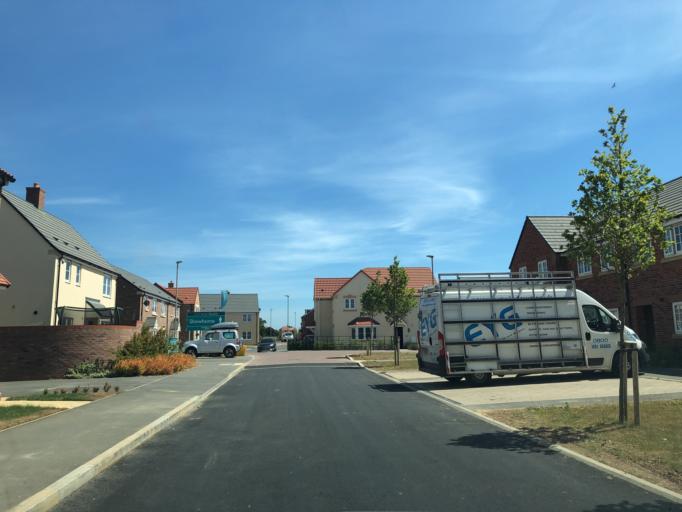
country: GB
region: England
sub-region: North Yorkshire
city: Scarborough
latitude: 54.2472
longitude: -0.3877
